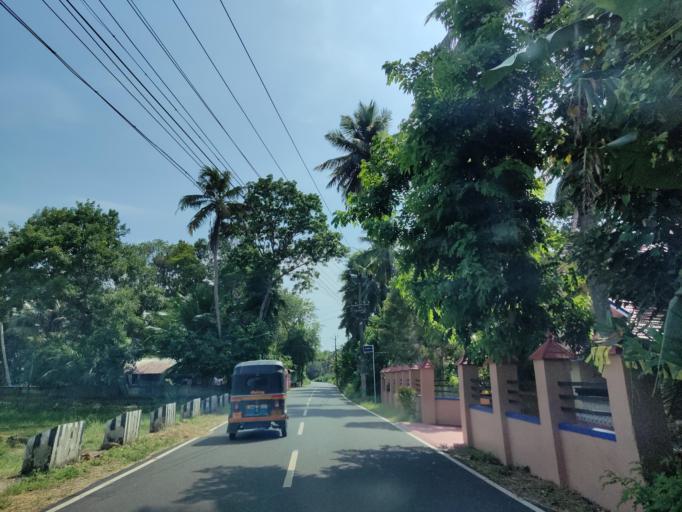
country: IN
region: Kerala
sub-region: Alappuzha
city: Mavelikara
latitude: 9.3278
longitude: 76.4746
